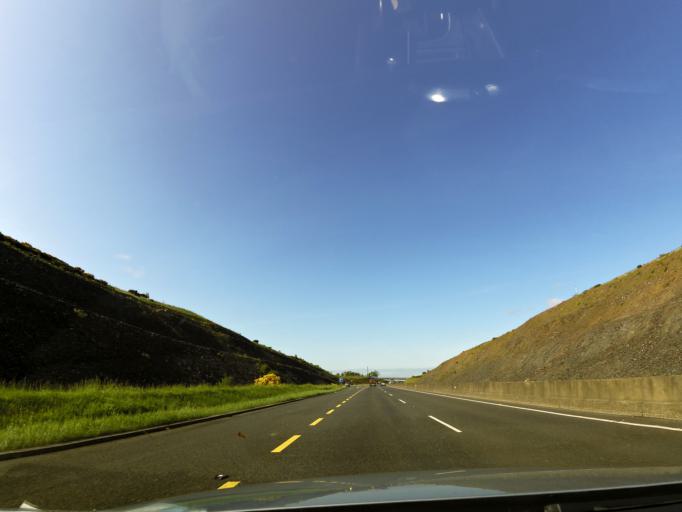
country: IE
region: Munster
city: Ballina
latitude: 52.7690
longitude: -8.3870
